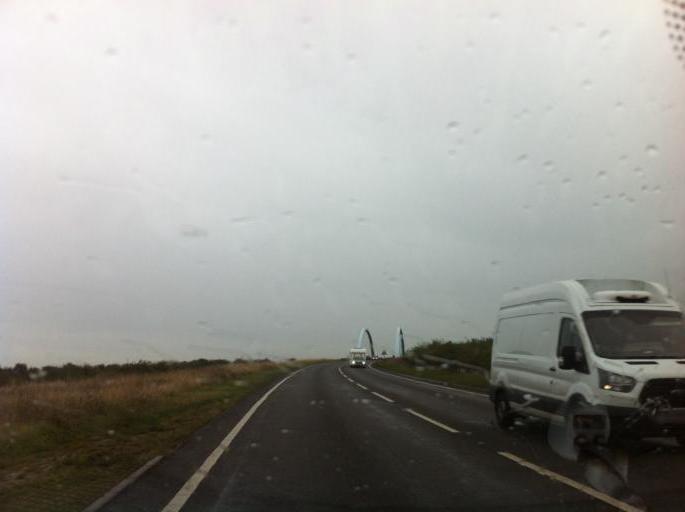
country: GB
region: England
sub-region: Peterborough
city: Eye
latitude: 52.6114
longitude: -0.2137
